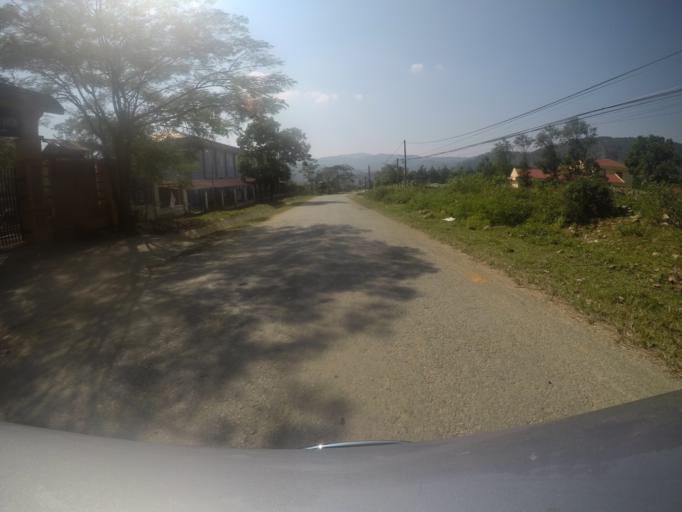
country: VN
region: Lai Chau
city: Than Uyen
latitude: 22.0167
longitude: 103.9197
